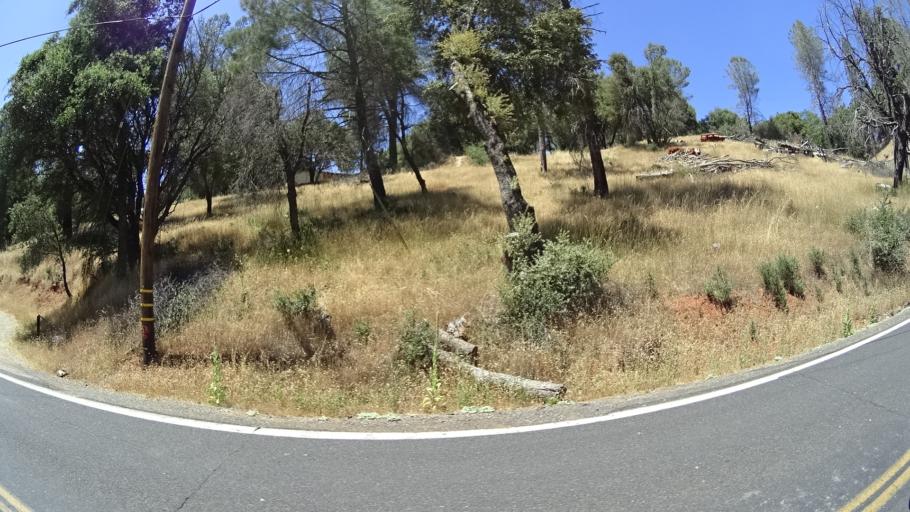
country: US
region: California
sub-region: Calaveras County
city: Mountain Ranch
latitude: 38.2791
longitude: -120.5067
